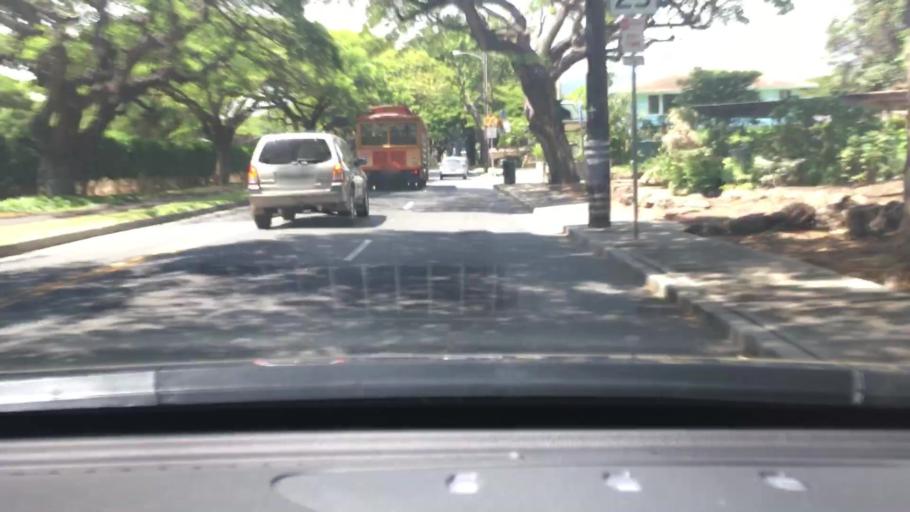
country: US
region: Hawaii
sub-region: Honolulu County
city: Honolulu
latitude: 21.2697
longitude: -157.8159
